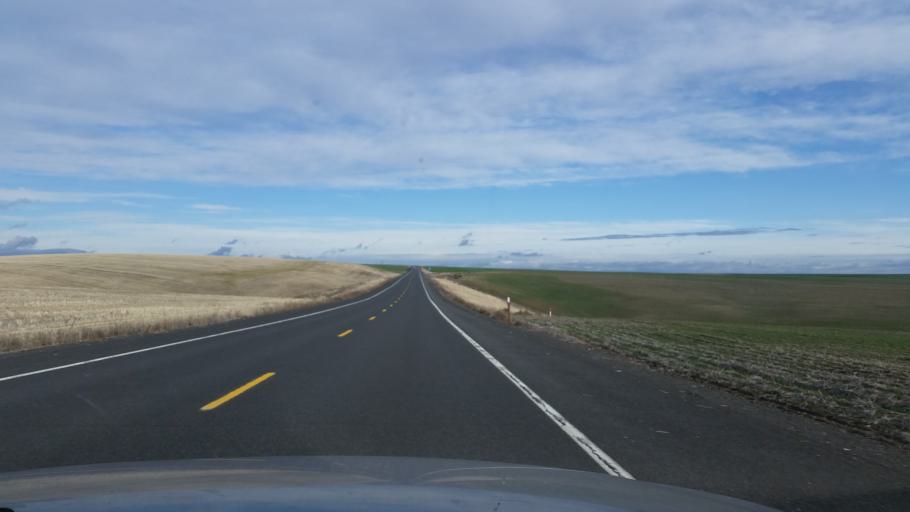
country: US
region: Washington
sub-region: Adams County
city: Ritzville
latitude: 47.3998
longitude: -118.3944
